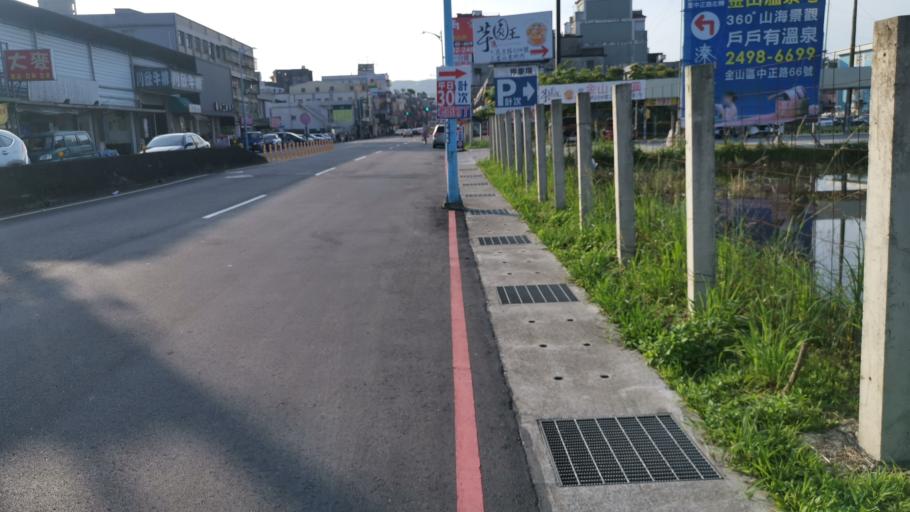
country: TW
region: Taiwan
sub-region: Keelung
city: Keelung
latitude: 25.2183
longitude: 121.6409
